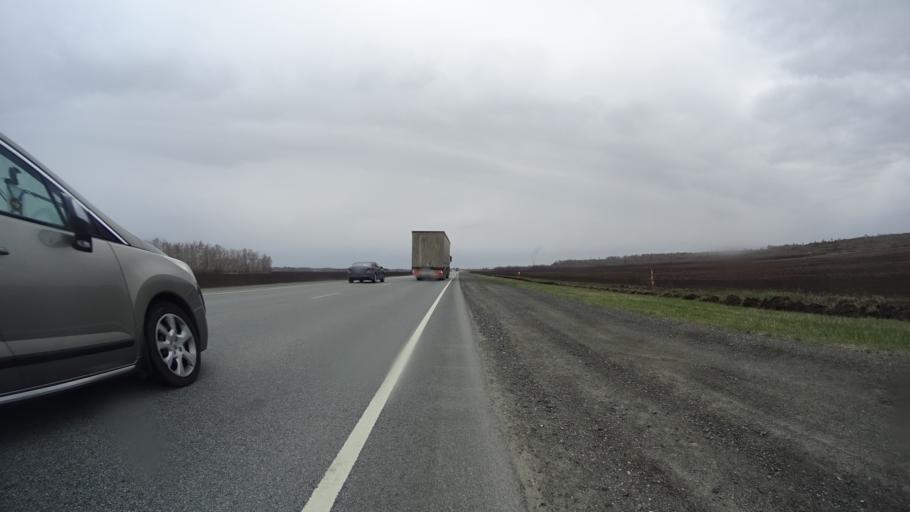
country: RU
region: Chelyabinsk
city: Krasnogorskiy
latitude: 54.5767
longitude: 61.2914
